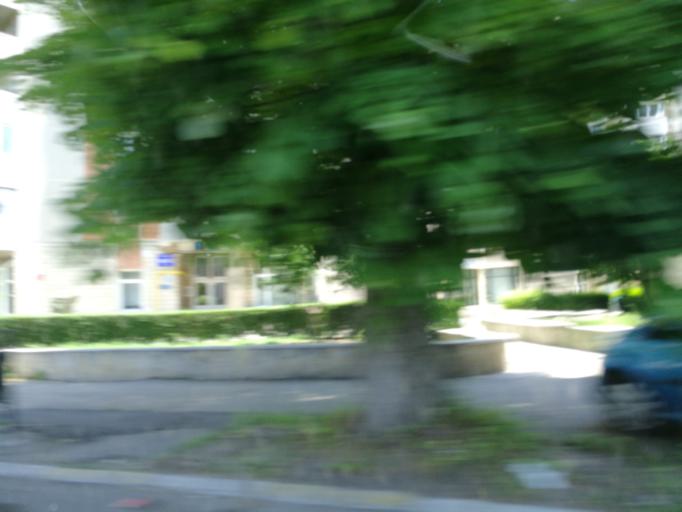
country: RO
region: Constanta
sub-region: Municipiul Constanta
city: Constanta
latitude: 44.1885
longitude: 28.6509
